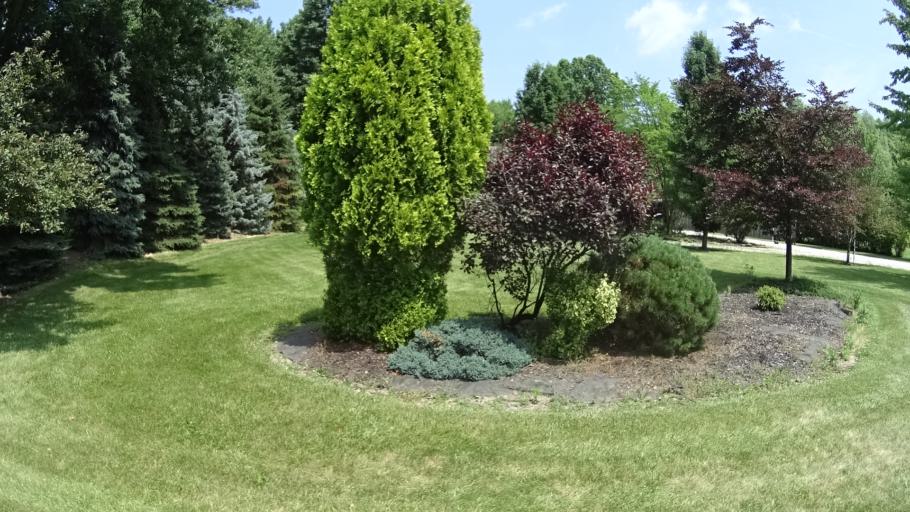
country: US
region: Ohio
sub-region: Lorain County
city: Vermilion
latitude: 41.3877
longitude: -82.3868
